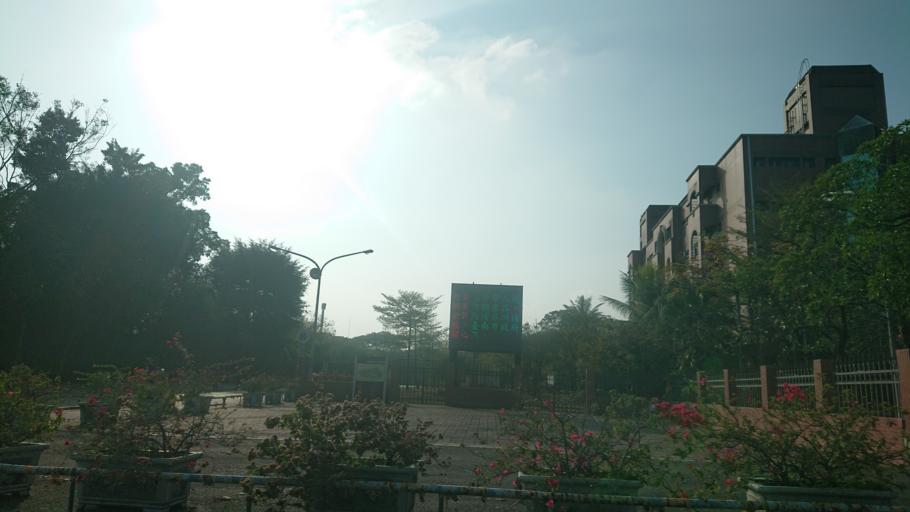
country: TW
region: Taiwan
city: Xinying
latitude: 23.1910
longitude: 120.2713
